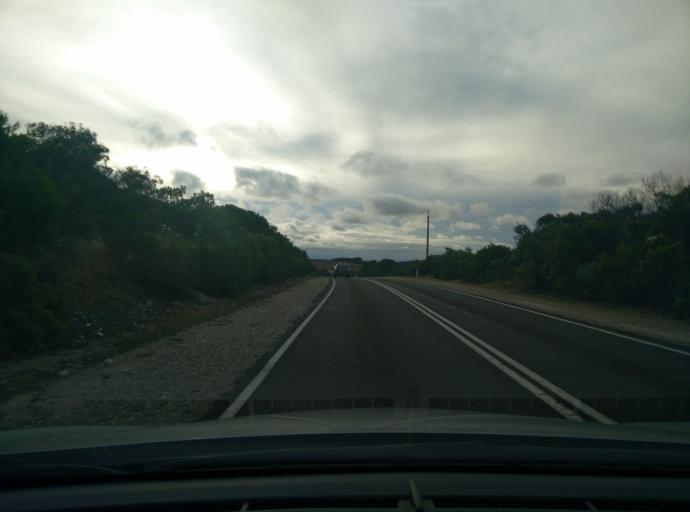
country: AU
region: South Australia
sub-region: Kangaroo Island
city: Kingscote
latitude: -35.8358
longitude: 137.7901
